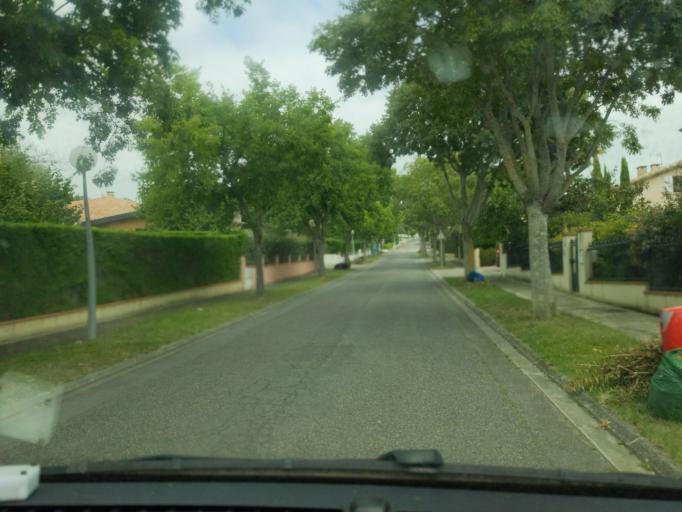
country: FR
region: Midi-Pyrenees
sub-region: Departement de la Haute-Garonne
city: Labege
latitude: 43.5285
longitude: 1.5390
